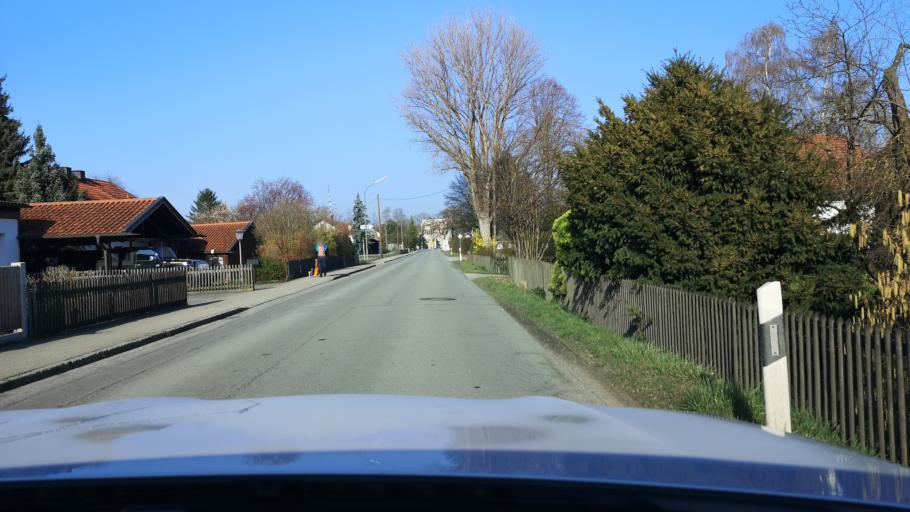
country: DE
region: Bavaria
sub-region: Upper Bavaria
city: Finsing
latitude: 48.2202
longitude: 11.8065
